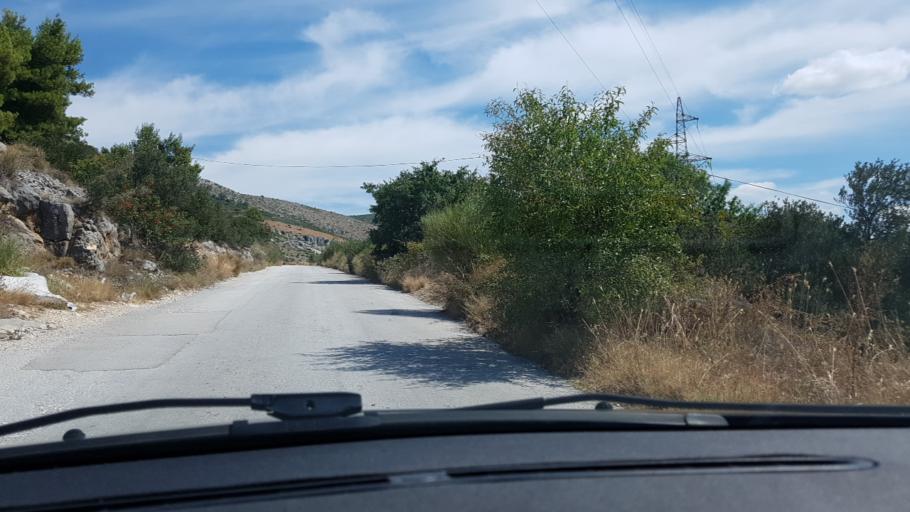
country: HR
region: Splitsko-Dalmatinska
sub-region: Grad Trogir
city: Trogir
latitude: 43.5265
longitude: 16.2283
